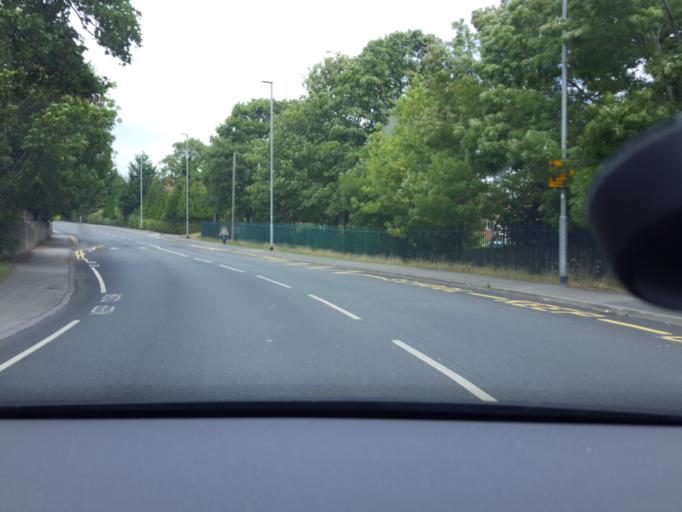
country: GB
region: England
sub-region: City and Borough of Leeds
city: Leeds
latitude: 53.7897
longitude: -1.5898
